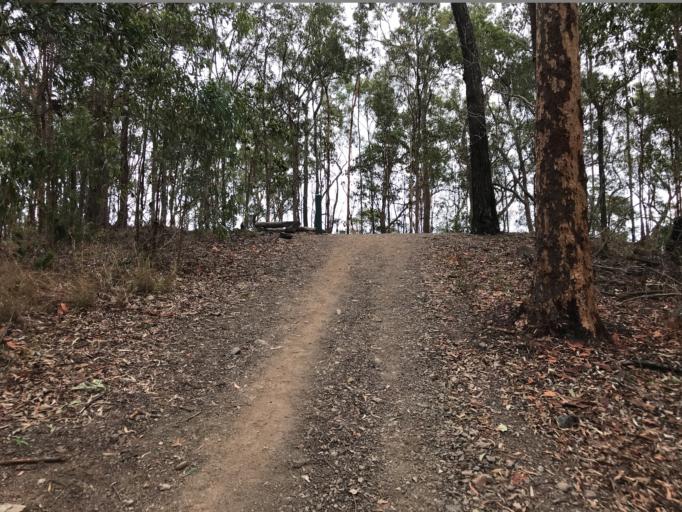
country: AU
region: Queensland
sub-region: Brisbane
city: Taringa
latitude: -27.4722
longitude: 152.9587
